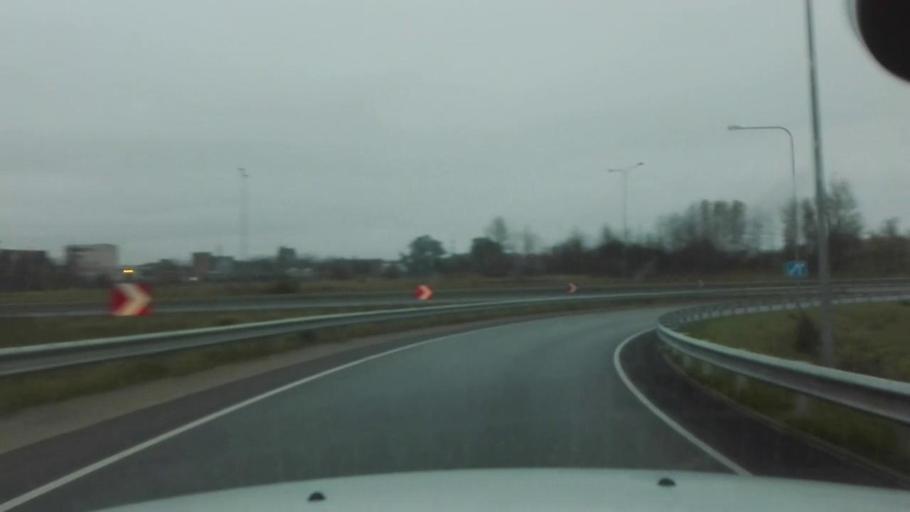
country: EE
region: Harju
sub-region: Joelaehtme vald
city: Loo
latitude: 59.4568
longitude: 24.9860
